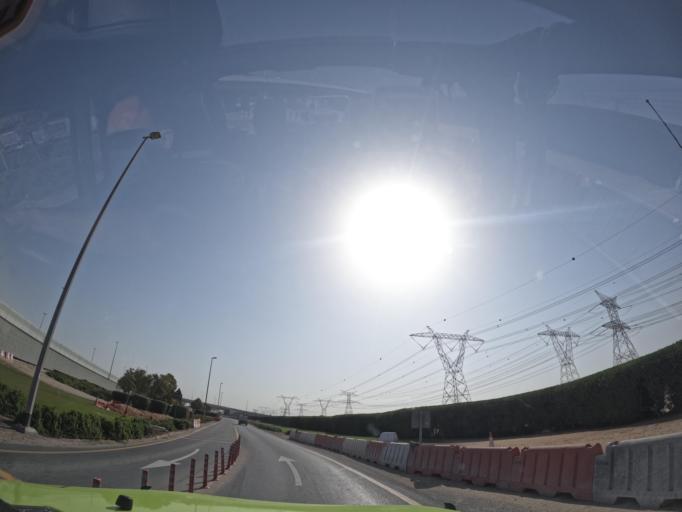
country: AE
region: Dubai
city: Dubai
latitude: 25.1701
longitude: 55.3151
